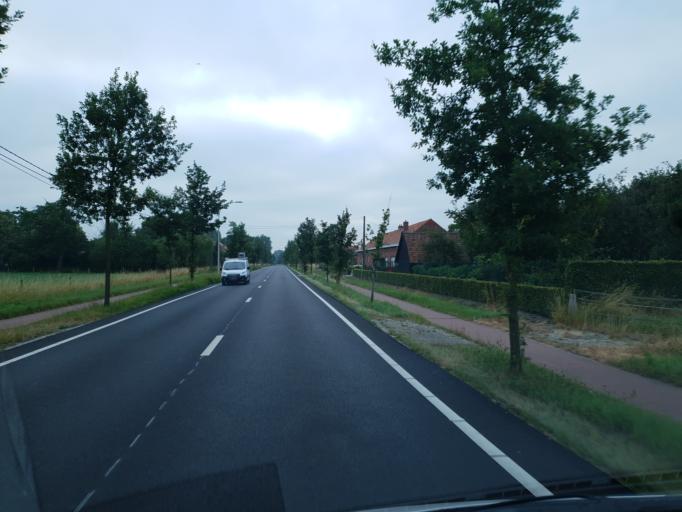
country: BE
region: Flanders
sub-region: Provincie Antwerpen
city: Brecht
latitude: 51.3595
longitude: 4.6981
